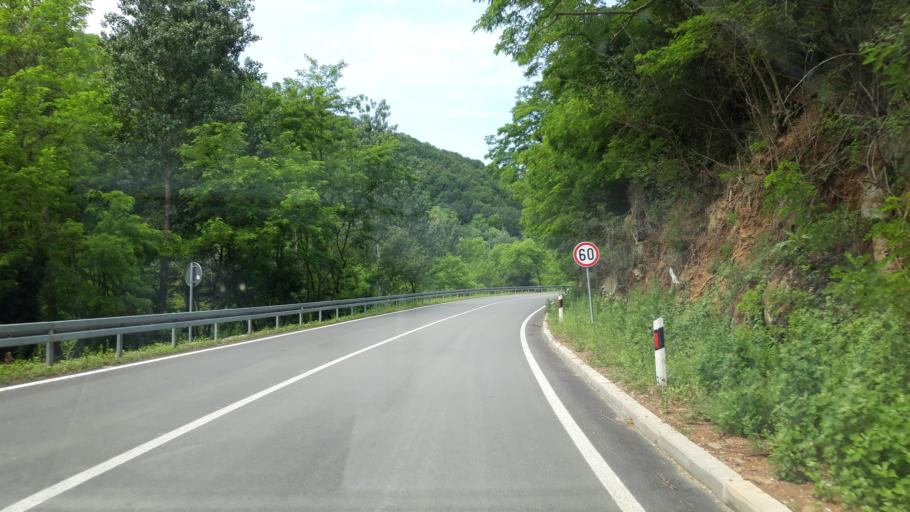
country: RS
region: Central Serbia
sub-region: Jablanicki Okrug
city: Vlasotince
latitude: 42.9767
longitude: 22.2529
